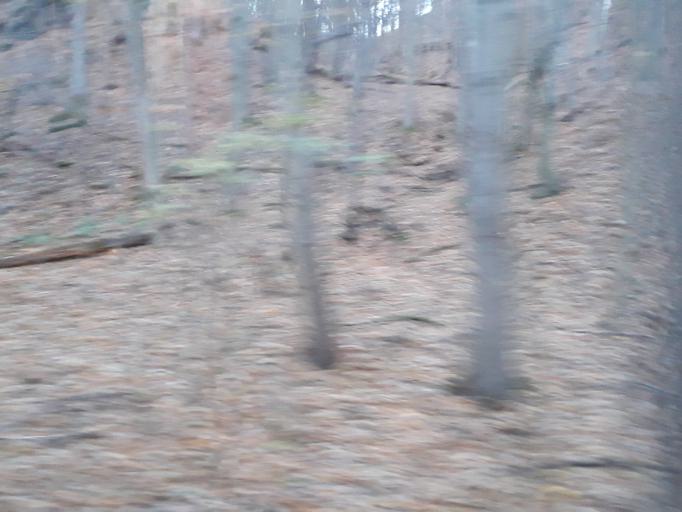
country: DE
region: Saxony
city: Reinhardtsgrimma
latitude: 50.9162
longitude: 13.7860
